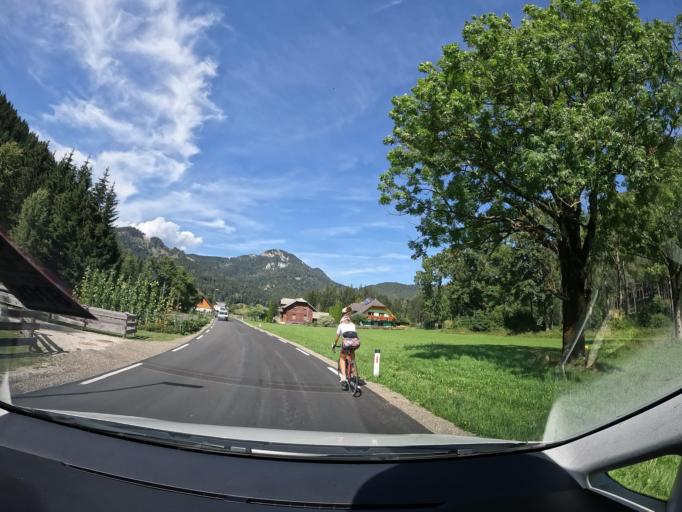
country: AT
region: Carinthia
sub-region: Politischer Bezirk Feldkirchen
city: Feldkirchen in Karnten
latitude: 46.6943
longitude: 14.1219
